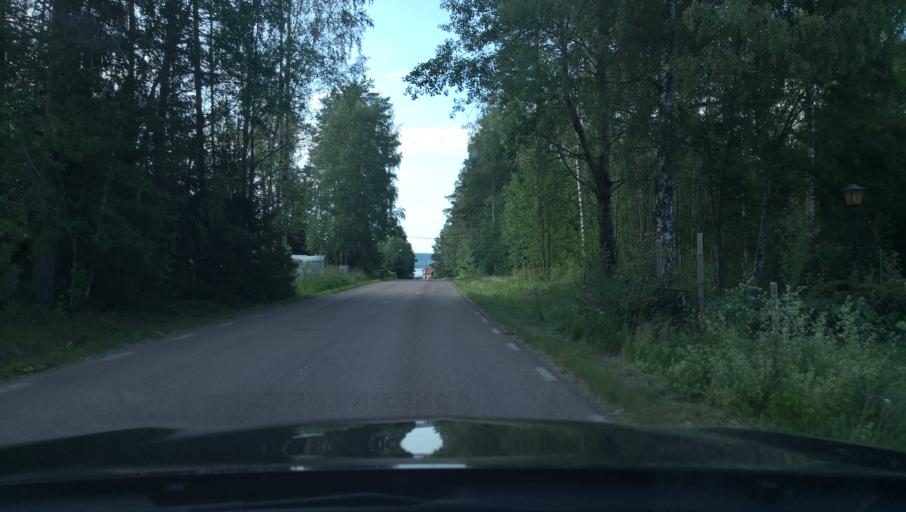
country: SE
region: Dalarna
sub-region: Ludvika Kommun
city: Ludvika
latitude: 60.0685
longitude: 15.2548
